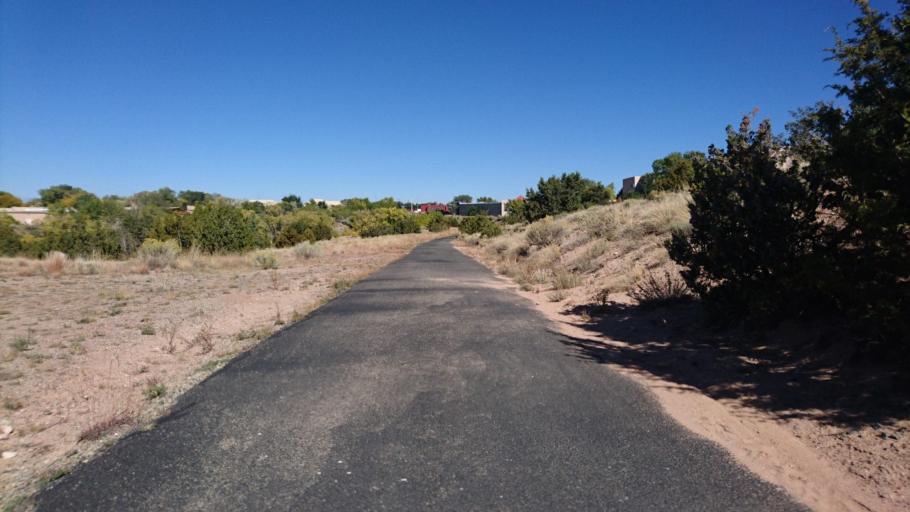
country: US
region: New Mexico
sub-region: Santa Fe County
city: Santa Fe
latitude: 35.6561
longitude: -105.9649
